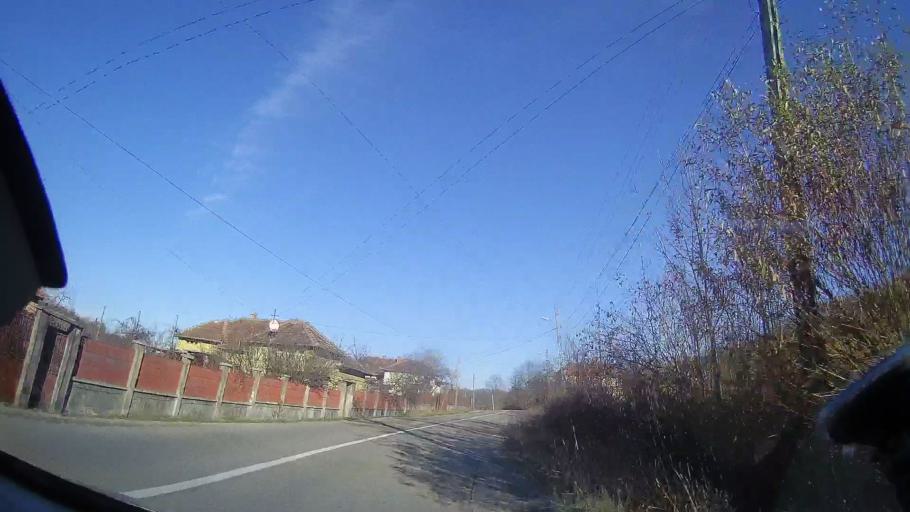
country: RO
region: Bihor
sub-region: Comuna Bratca
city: Bratca
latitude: 46.9349
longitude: 22.6034
